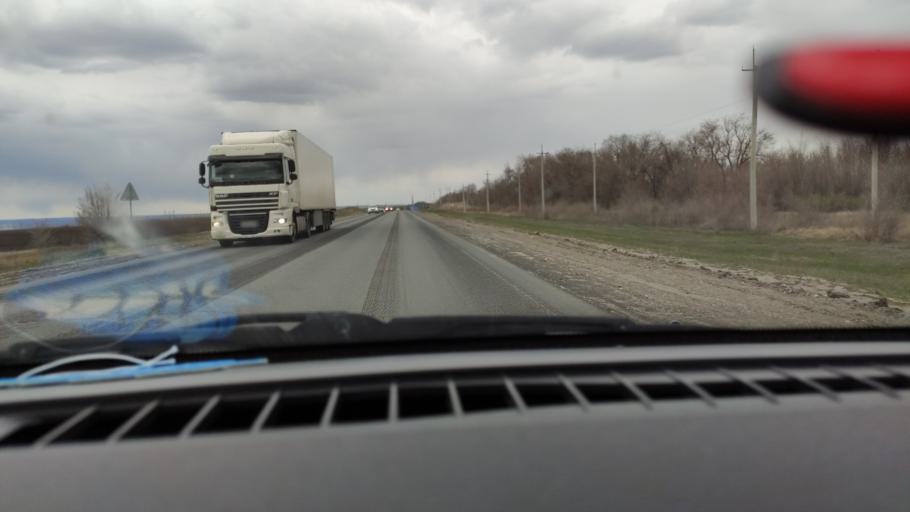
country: RU
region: Saratov
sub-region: Saratovskiy Rayon
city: Saratov
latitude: 51.7753
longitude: 46.0950
